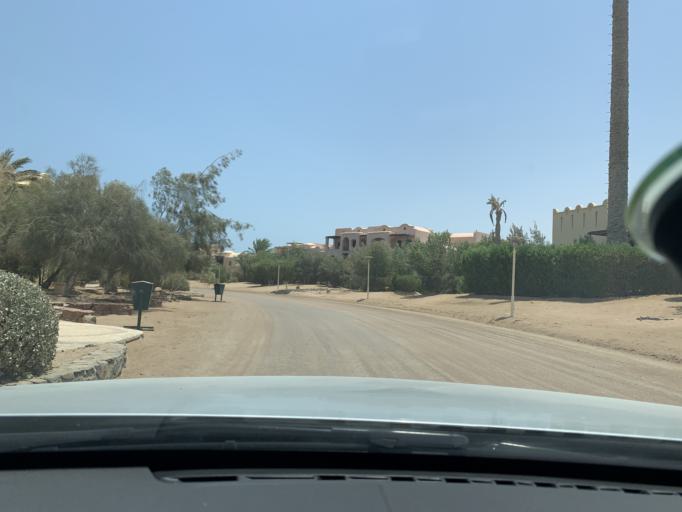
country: EG
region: Red Sea
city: El Gouna
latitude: 27.4015
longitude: 33.6728
